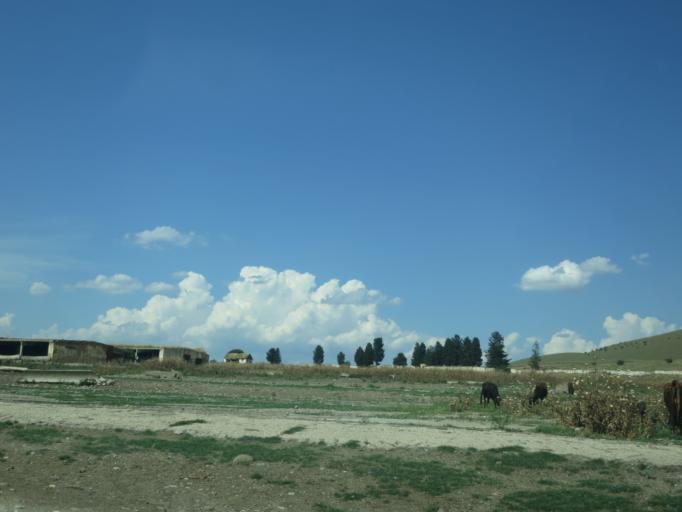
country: GE
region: Kvemo Kartli
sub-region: Gardabani
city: Gardabani
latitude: 41.4983
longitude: 45.1882
